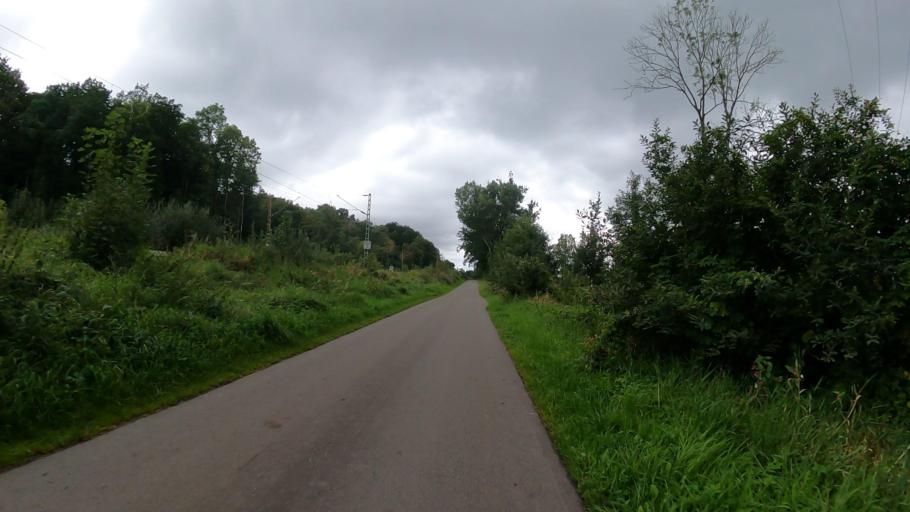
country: DE
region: Lower Saxony
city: Agathenburg
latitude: 53.5580
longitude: 9.5433
